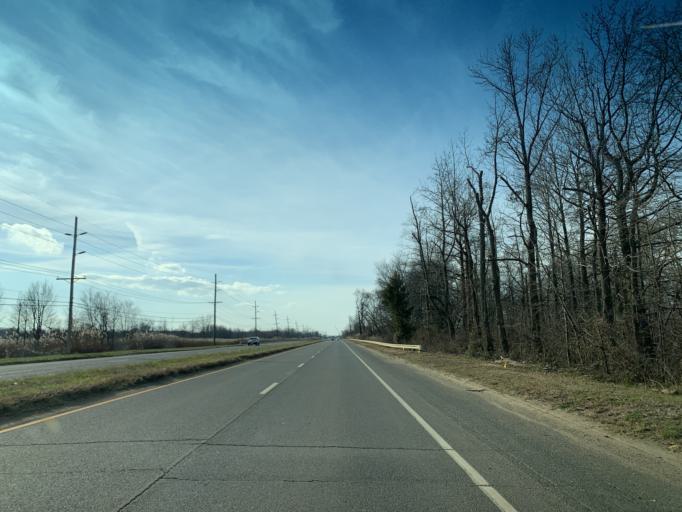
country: US
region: Pennsylvania
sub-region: Delaware County
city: Marcus Hook
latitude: 39.7918
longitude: -75.3825
